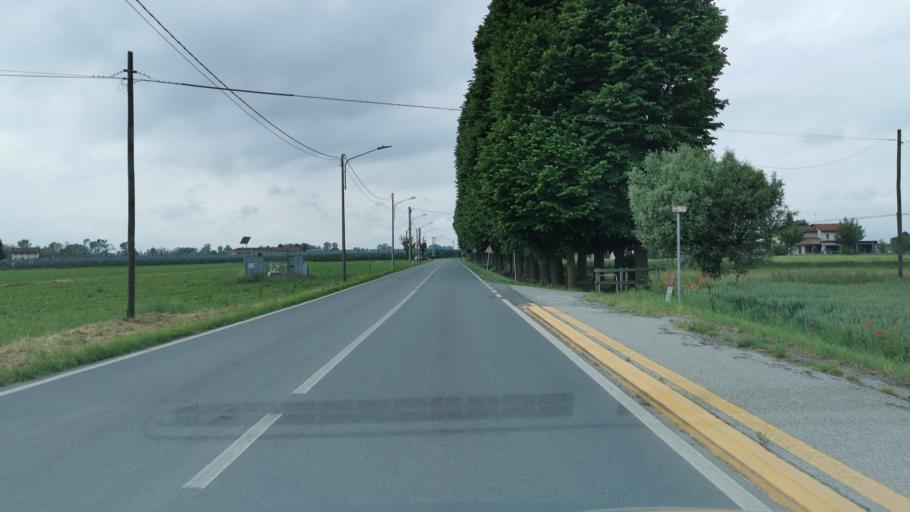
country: IT
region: Piedmont
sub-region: Provincia di Cuneo
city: Savigliano
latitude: 44.6294
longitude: 7.6398
